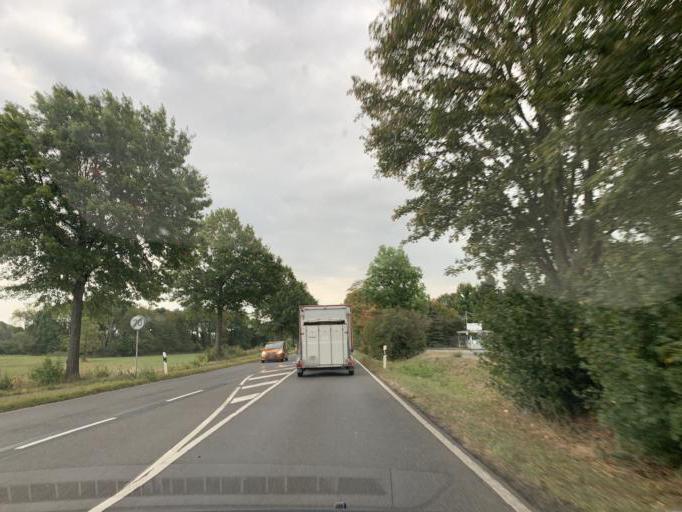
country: DE
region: North Rhine-Westphalia
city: Huckelhoven
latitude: 51.0306
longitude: 6.2195
